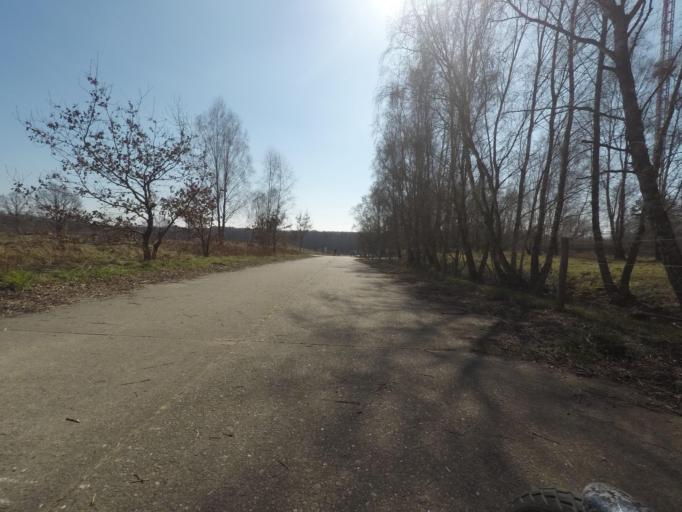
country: DE
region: Schleswig-Holstein
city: Stapelfeld
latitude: 53.6268
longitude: 10.1971
